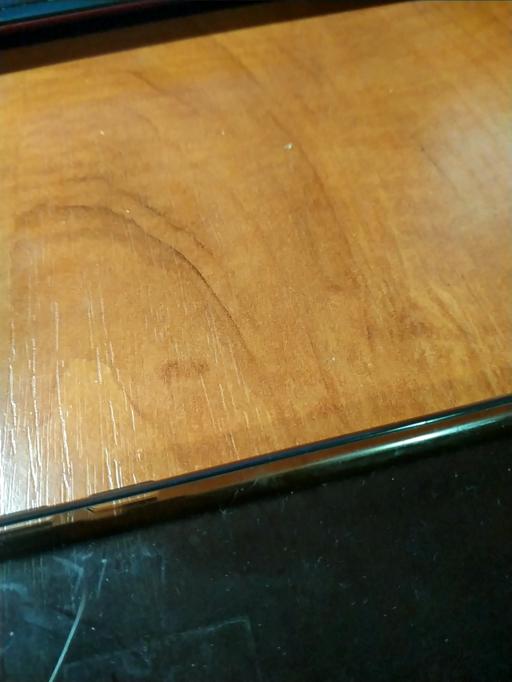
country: RU
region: Kaluga
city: Iznoski
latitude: 54.8844
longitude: 35.3633
